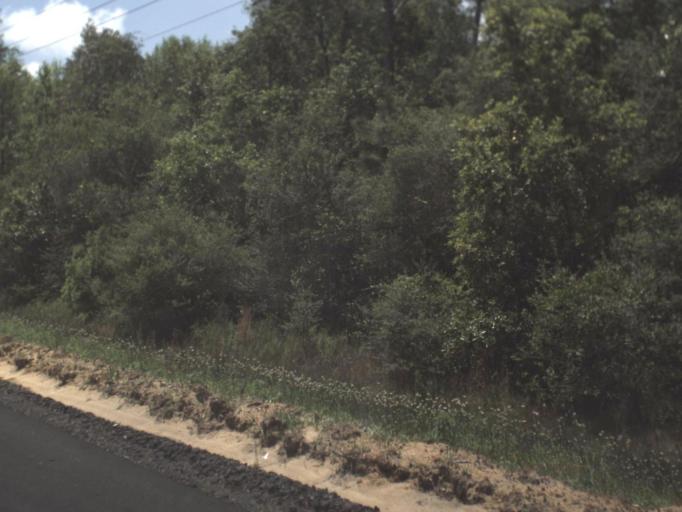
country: US
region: Florida
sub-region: Escambia County
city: Myrtle Grove
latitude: 30.4130
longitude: -87.3175
